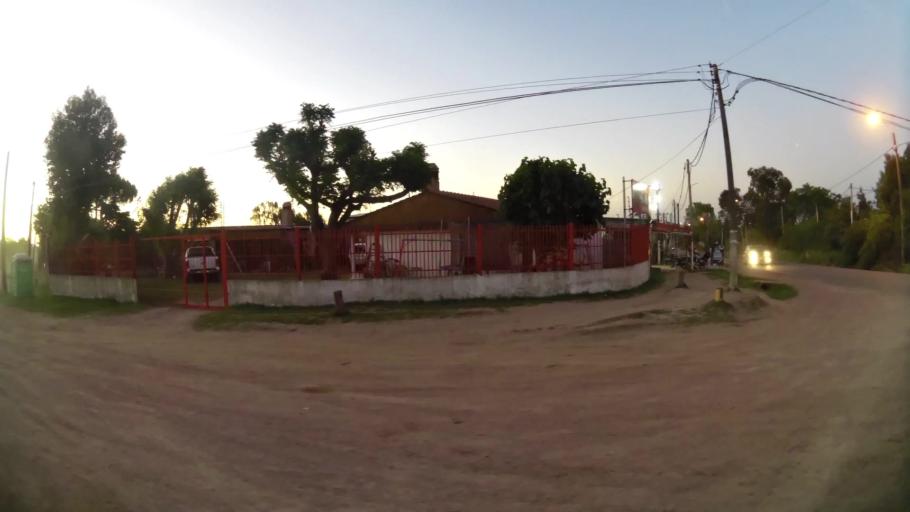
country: UY
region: Canelones
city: Colonia Nicolich
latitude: -34.8140
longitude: -55.9646
